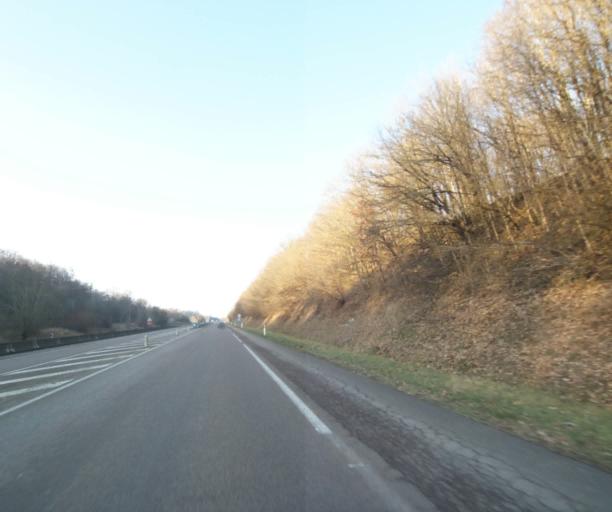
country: FR
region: Champagne-Ardenne
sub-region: Departement de la Haute-Marne
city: Chevillon
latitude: 48.5029
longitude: 5.1037
